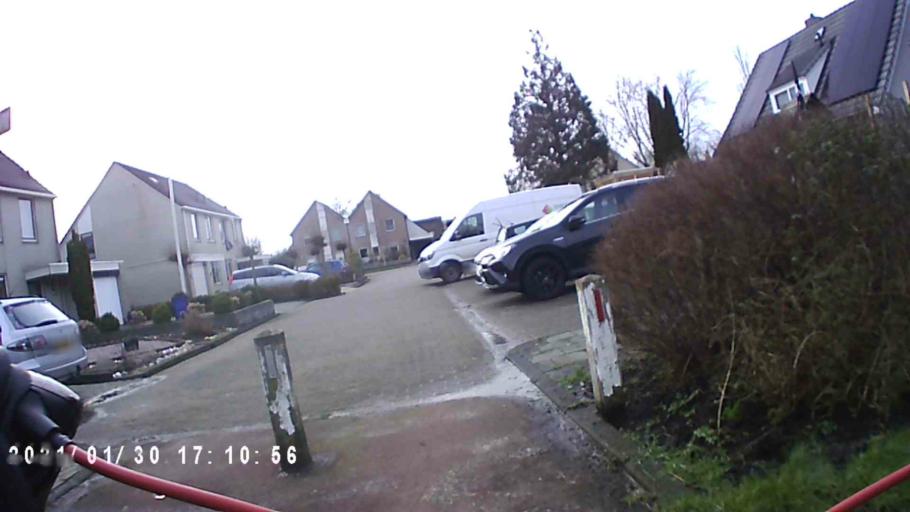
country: NL
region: Groningen
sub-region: Gemeente Leek
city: Leek
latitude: 53.1688
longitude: 6.3630
